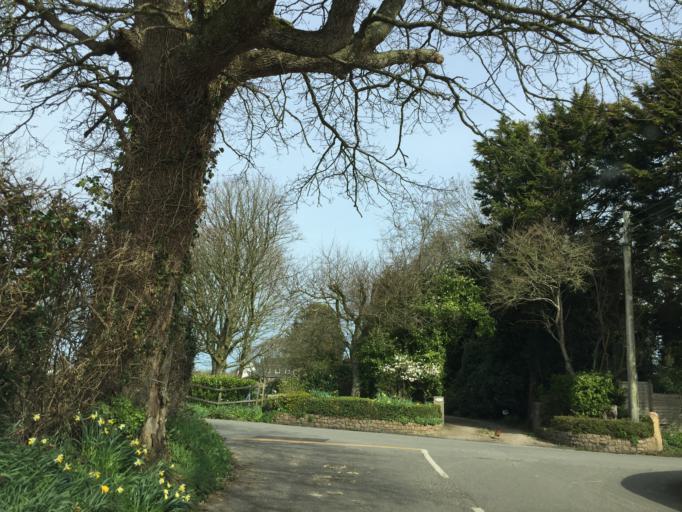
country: JE
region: St Helier
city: Saint Helier
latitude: 49.2277
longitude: -2.0589
